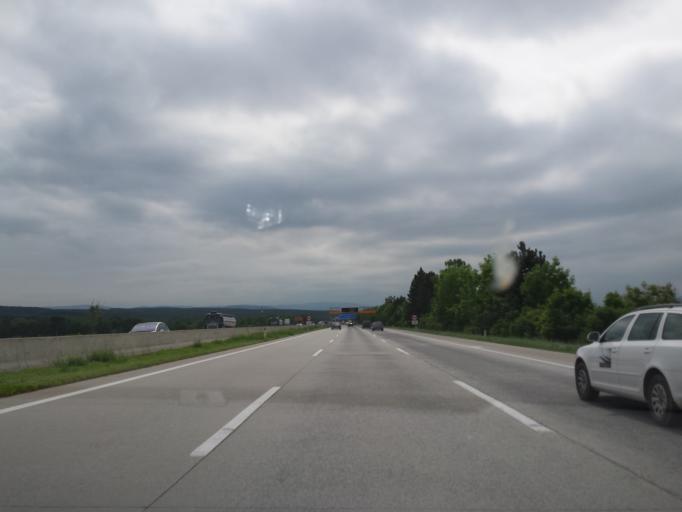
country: AT
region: Lower Austria
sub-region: Politischer Bezirk Neunkirchen
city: Breitenau
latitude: 47.7271
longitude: 16.1483
